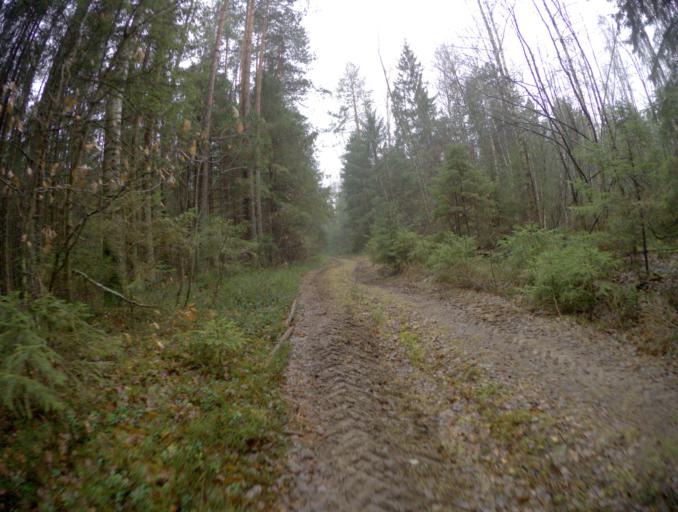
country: RU
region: Vladimir
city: Golovino
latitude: 56.0047
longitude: 40.4739
